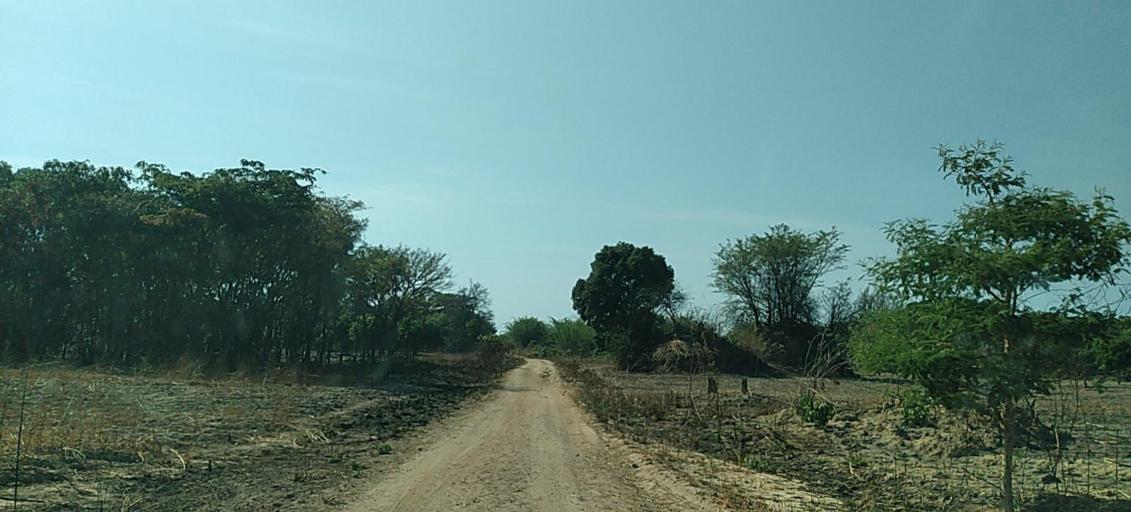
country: ZM
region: Copperbelt
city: Luanshya
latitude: -13.1951
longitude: 28.4825
